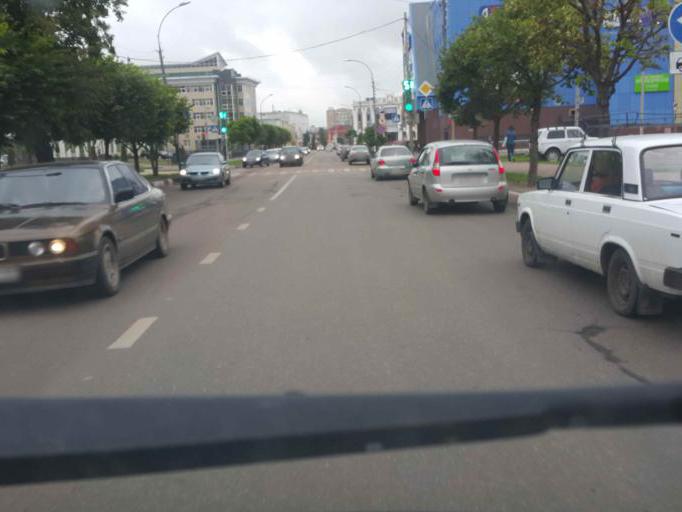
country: RU
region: Tambov
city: Tambov
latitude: 52.7185
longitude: 41.4534
